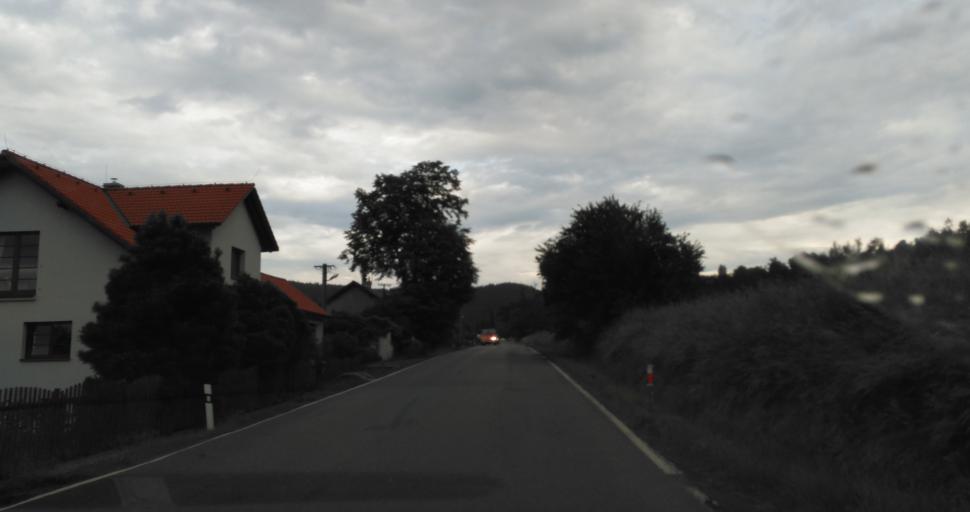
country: CZ
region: Central Bohemia
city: Jince
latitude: 49.7805
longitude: 13.9889
